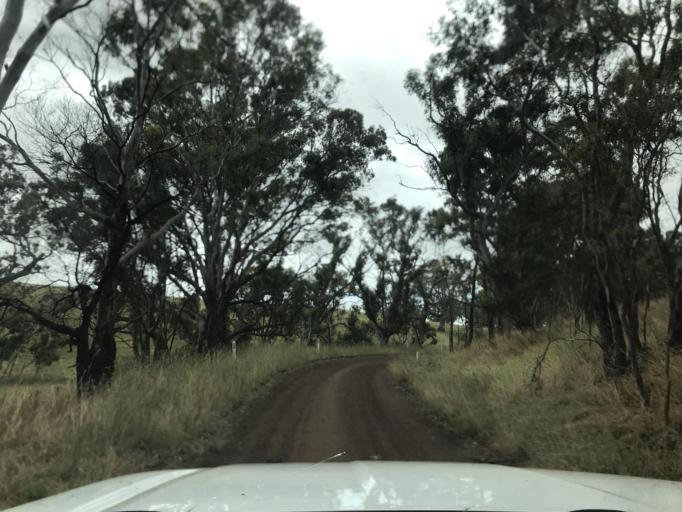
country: AU
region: South Australia
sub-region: Wattle Range
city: Penola
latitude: -37.2345
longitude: 141.4687
